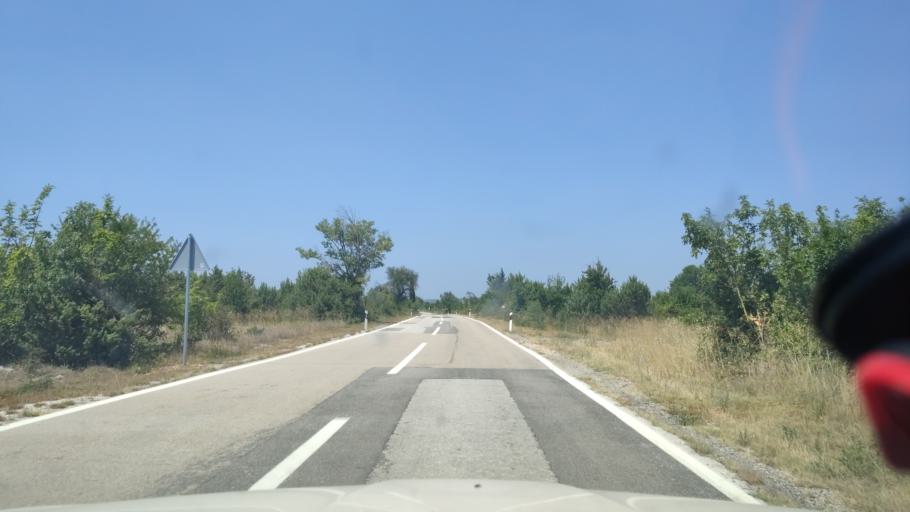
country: HR
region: Sibensko-Kniniska
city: Kistanje
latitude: 43.9759
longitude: 15.9387
